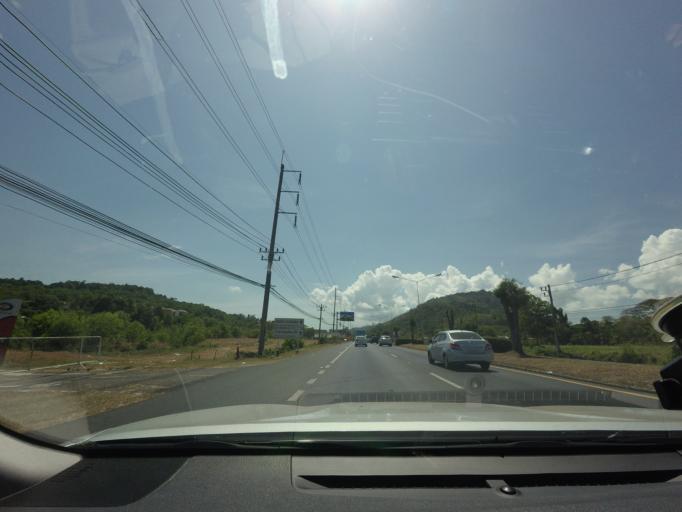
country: TH
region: Phuket
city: Ban Ko Kaeo
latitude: 7.9509
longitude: 98.3869
